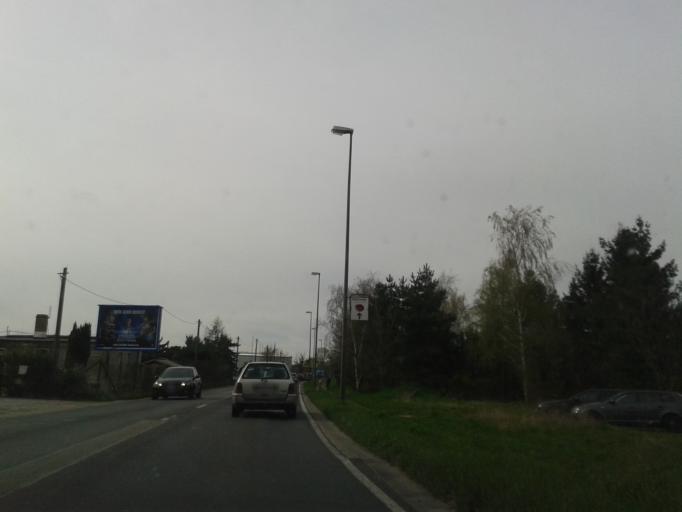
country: DE
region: Saxony
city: Radebeul
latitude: 51.0887
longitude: 13.6779
